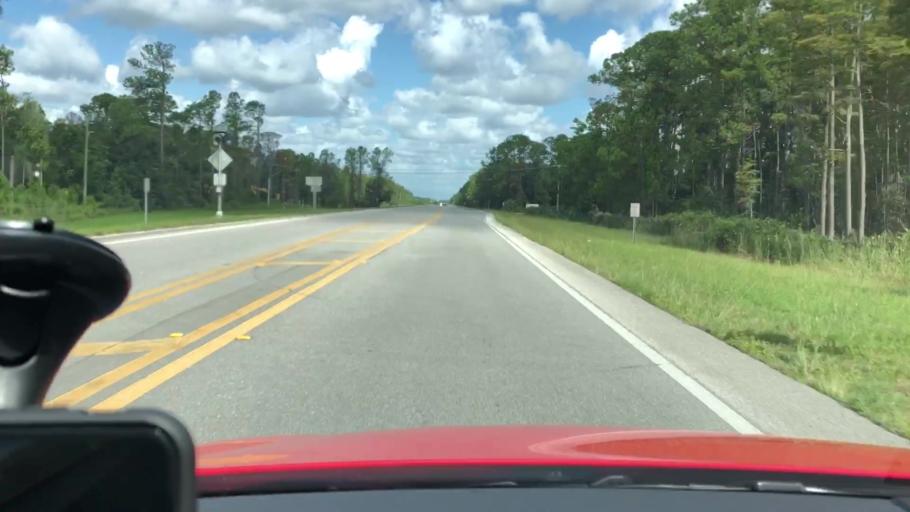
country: US
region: Florida
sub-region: Volusia County
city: Daytona Beach
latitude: 29.1771
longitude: -81.1197
